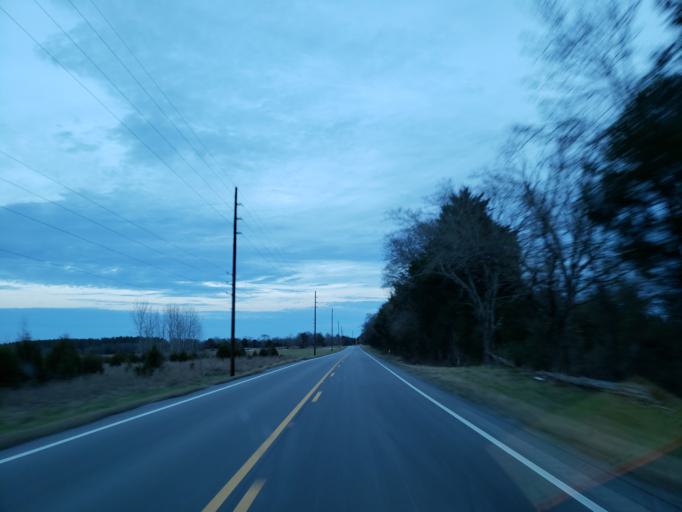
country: US
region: Alabama
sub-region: Sumter County
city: Livingston
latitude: 32.8103
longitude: -88.2867
